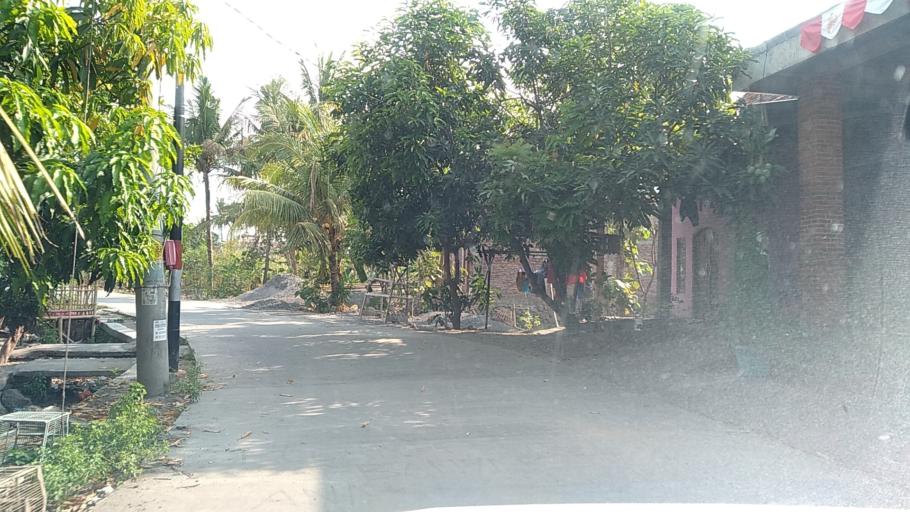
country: ID
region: Central Java
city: Mranggen
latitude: -6.9770
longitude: 110.5029
